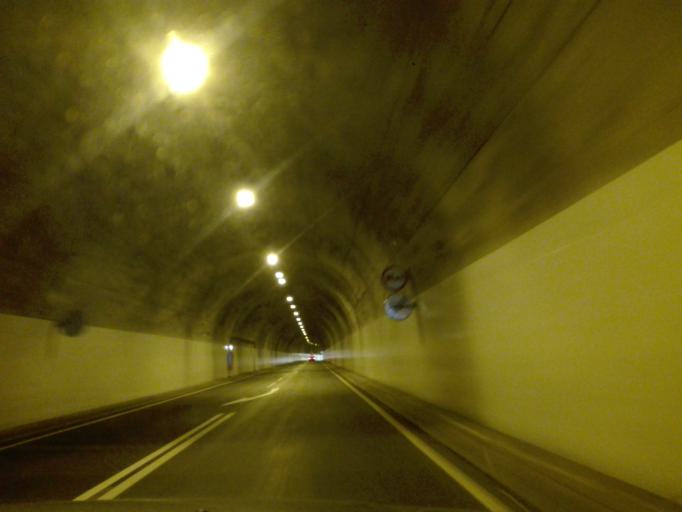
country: PT
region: Madeira
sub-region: Santana
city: Santana
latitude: 32.7668
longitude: -16.8387
